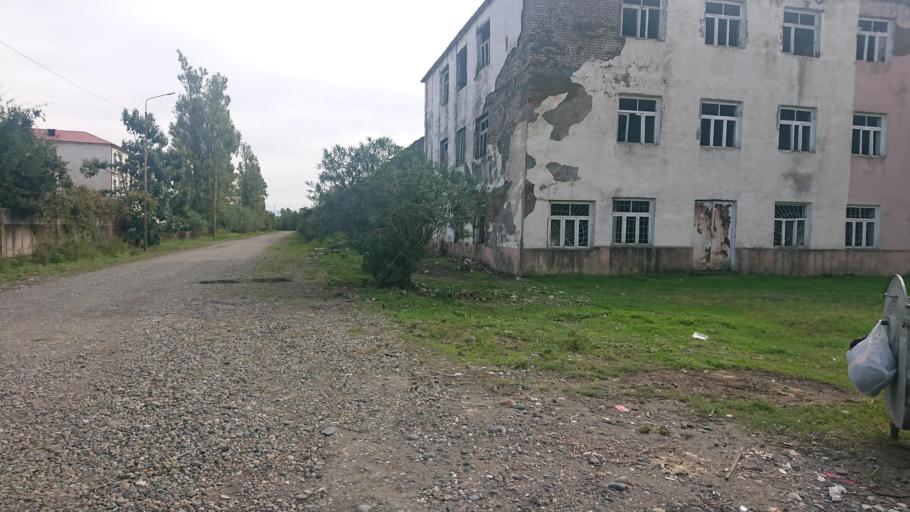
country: GE
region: Samegrelo and Zemo Svaneti
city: P'ot'i
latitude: 42.1247
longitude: 41.6892
